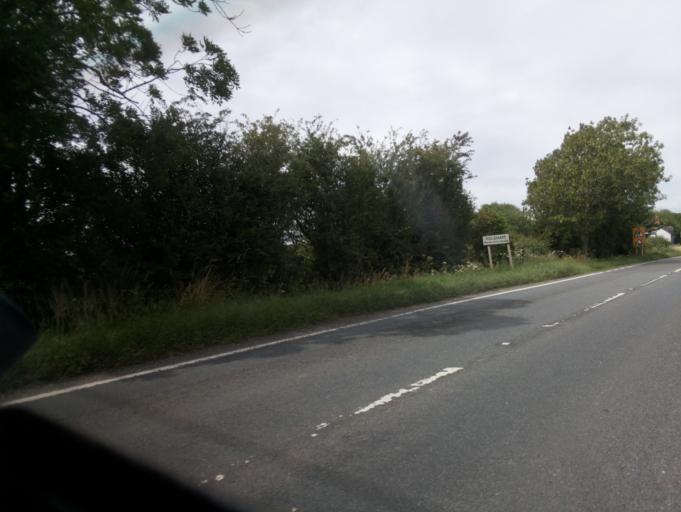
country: GB
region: England
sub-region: Somerset
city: Glastonbury
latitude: 51.1741
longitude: -2.6944
